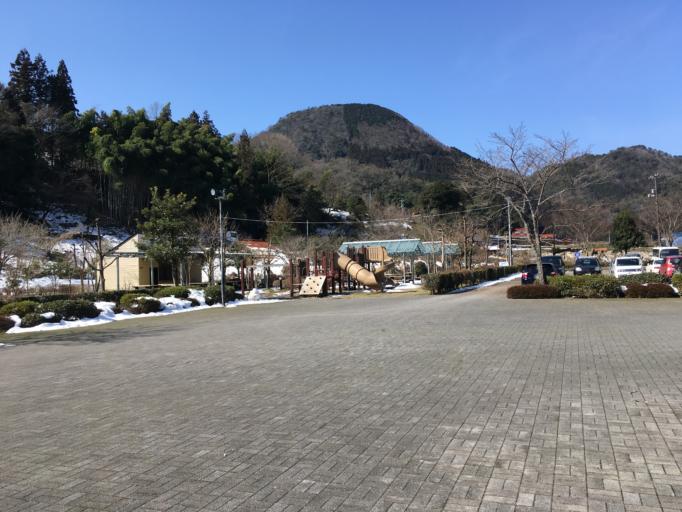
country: JP
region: Shimane
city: Masuda
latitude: 34.4506
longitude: 131.7601
